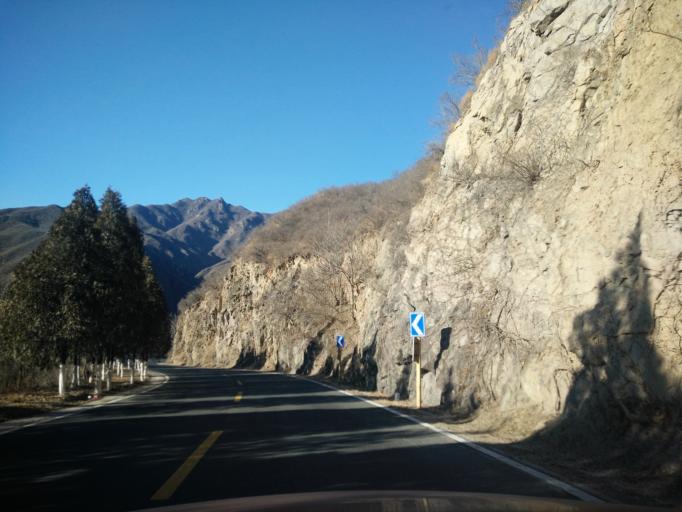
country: CN
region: Beijing
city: Wangping
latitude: 40.0035
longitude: 115.9460
